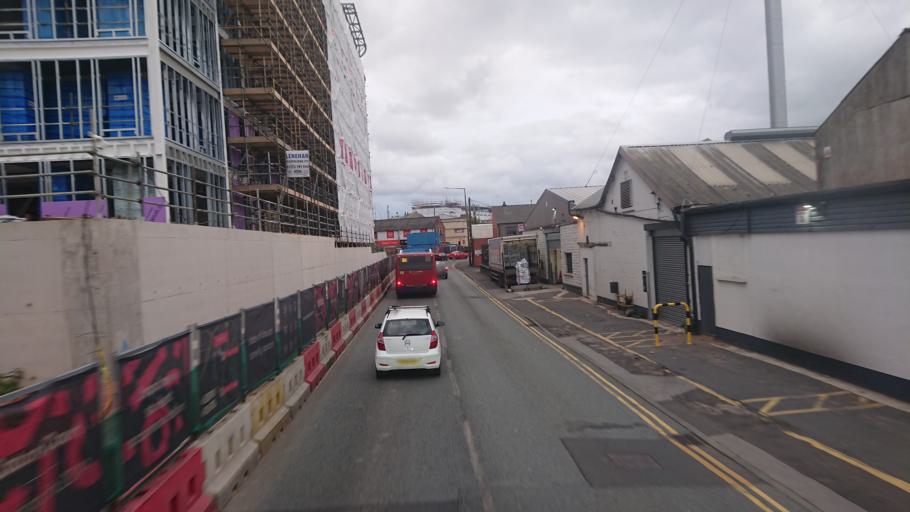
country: GB
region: England
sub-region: Lancashire
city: Lancaster
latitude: 54.0530
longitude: -2.7945
